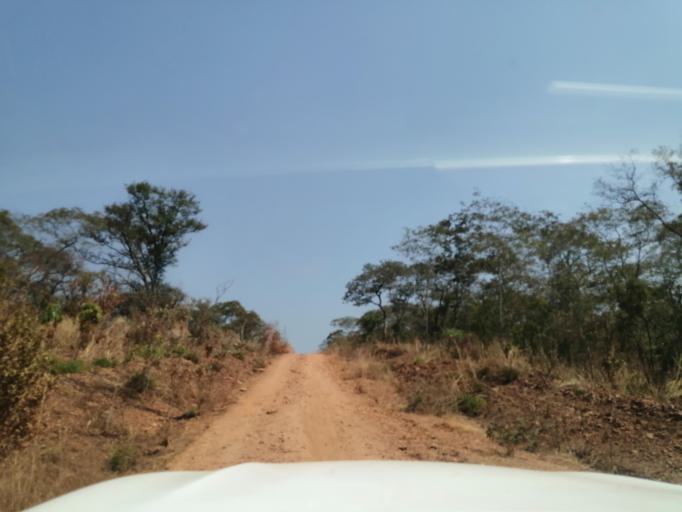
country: ZM
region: Eastern
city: Nyimba
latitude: -14.3196
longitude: 30.0441
